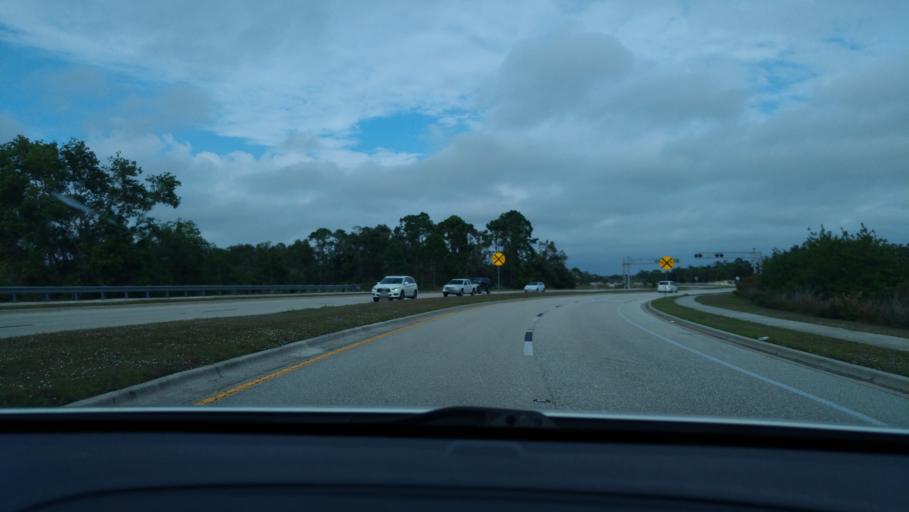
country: US
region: Florida
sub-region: Lee County
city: Estero
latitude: 26.4222
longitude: -81.8065
